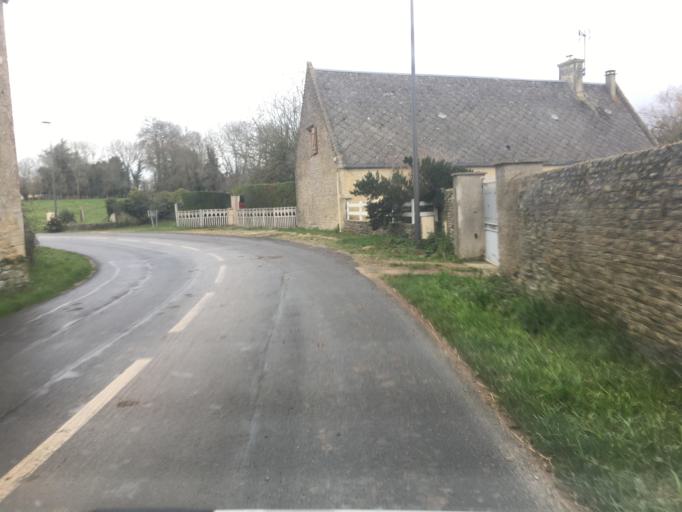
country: FR
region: Lower Normandy
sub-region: Departement du Calvados
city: Saint-Vigor-le-Grand
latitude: 49.3371
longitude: -0.6559
